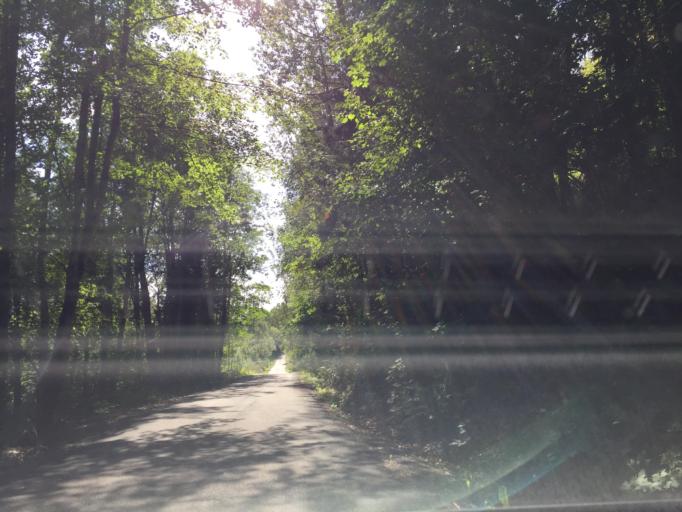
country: NO
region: Vestfold
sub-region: Hof
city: Hof
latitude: 59.4679
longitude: 10.1448
